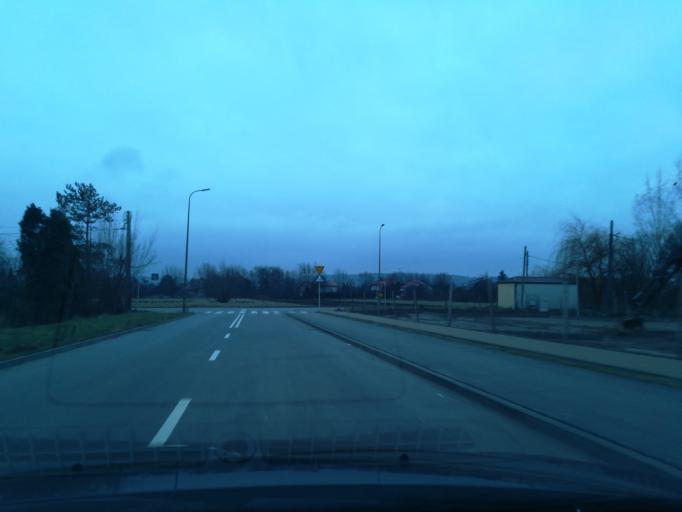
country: PL
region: Subcarpathian Voivodeship
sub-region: Rzeszow
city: Rzeszow
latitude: 50.0109
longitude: 22.0095
